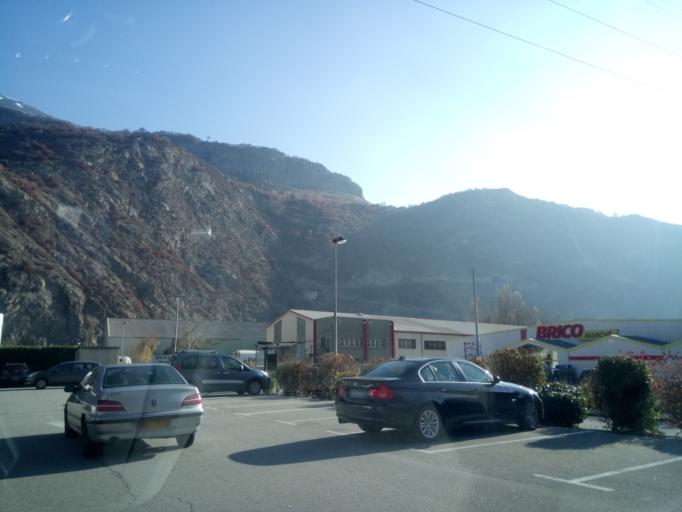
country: FR
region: Rhone-Alpes
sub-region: Departement de la Savoie
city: Saint-Jean-de-Maurienne
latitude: 45.2908
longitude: 6.3574
